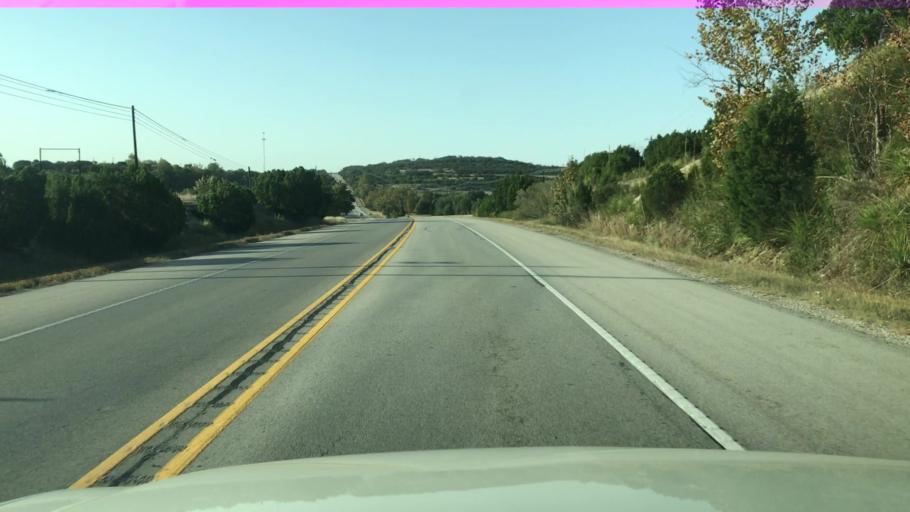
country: US
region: Texas
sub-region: Blanco County
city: Johnson City
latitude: 30.1898
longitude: -98.3777
